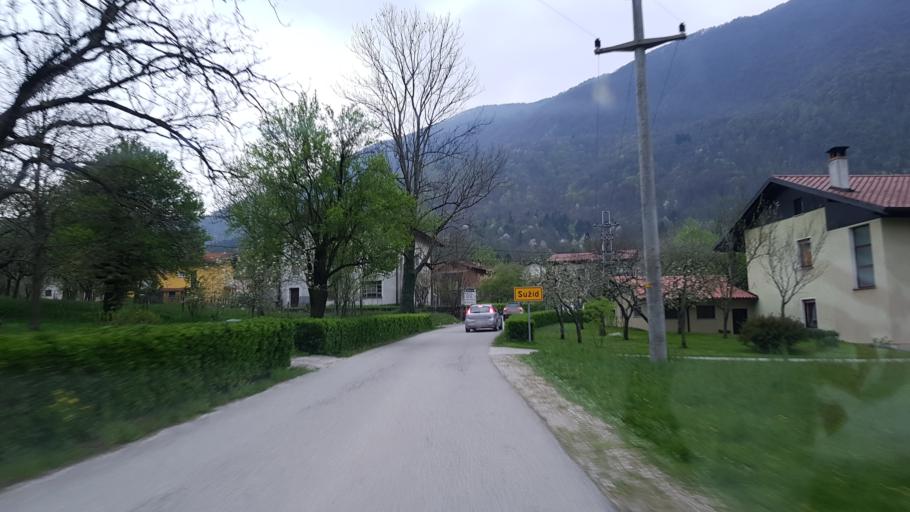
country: SI
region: Kobarid
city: Kobarid
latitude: 46.2437
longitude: 13.5528
